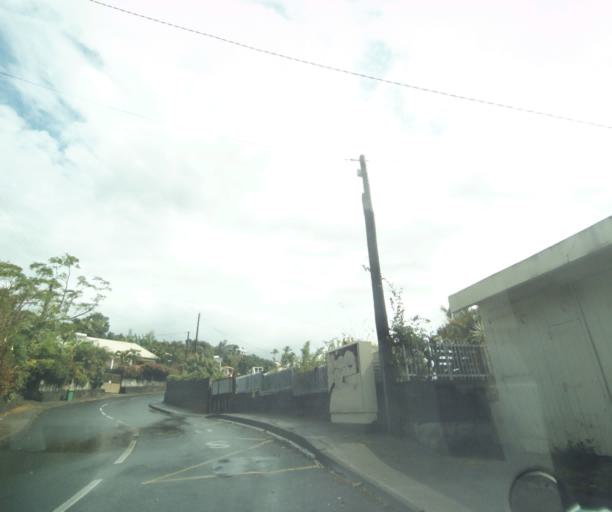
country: RE
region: Reunion
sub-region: Reunion
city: Saint-Paul
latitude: -21.0014
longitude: 55.3239
